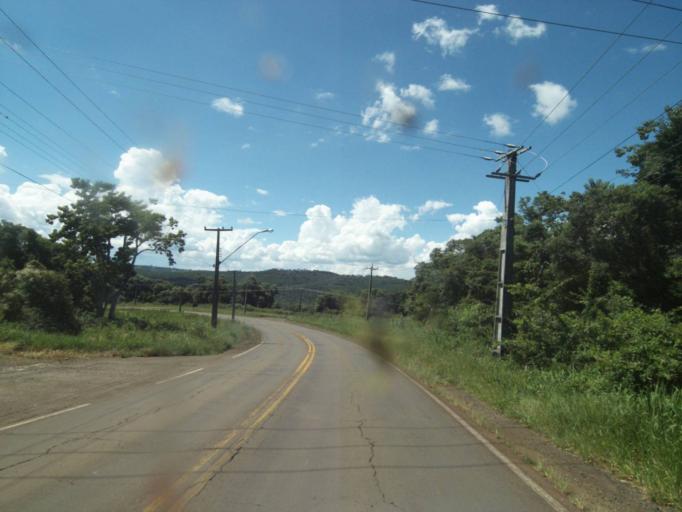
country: BR
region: Parana
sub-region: Chopinzinho
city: Chopinzinho
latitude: -25.7809
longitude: -52.1011
